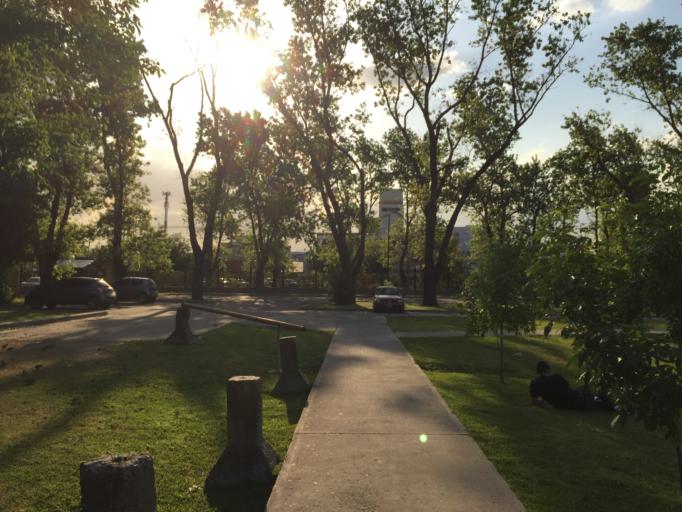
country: AR
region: Buenos Aires
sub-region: Partido de Lomas de Zamora
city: Lomas de Zamora
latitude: -34.7352
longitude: -58.3935
